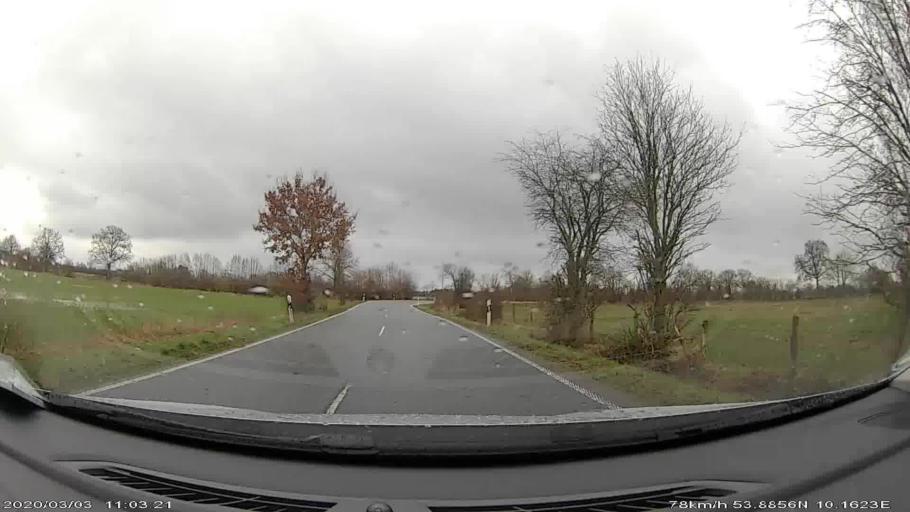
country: DE
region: Schleswig-Holstein
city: Todesfelde
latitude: 53.8827
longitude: 10.1602
